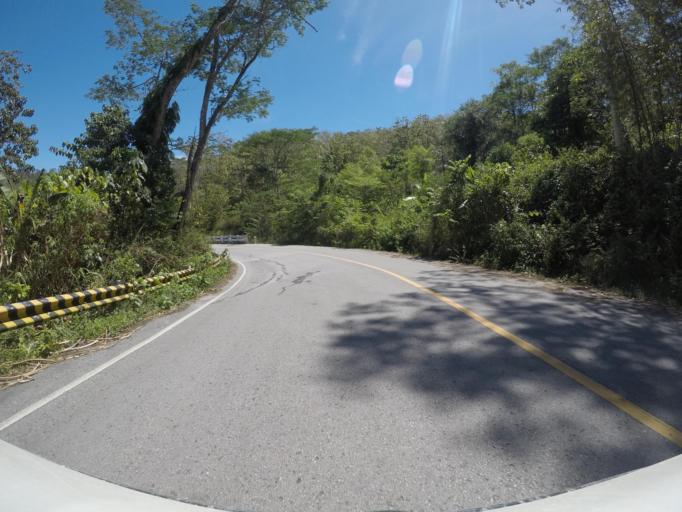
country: TL
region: Manatuto
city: Manatuto
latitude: -8.8208
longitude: 125.9791
